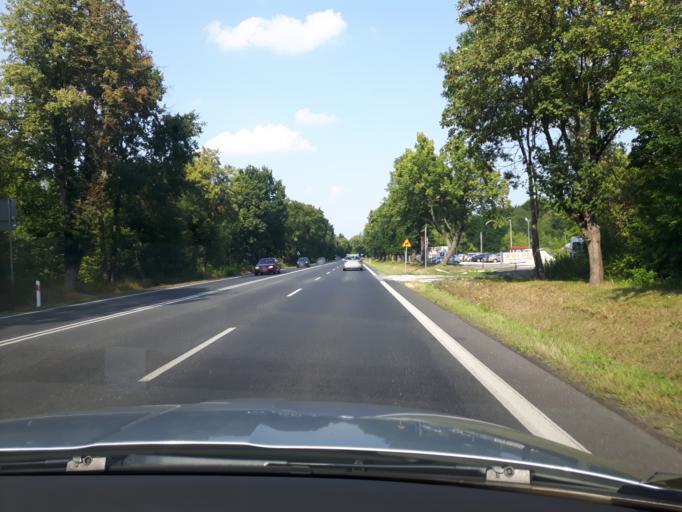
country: PL
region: Masovian Voivodeship
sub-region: Powiat nowodworski
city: Zakroczym
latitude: 52.4442
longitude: 20.6634
